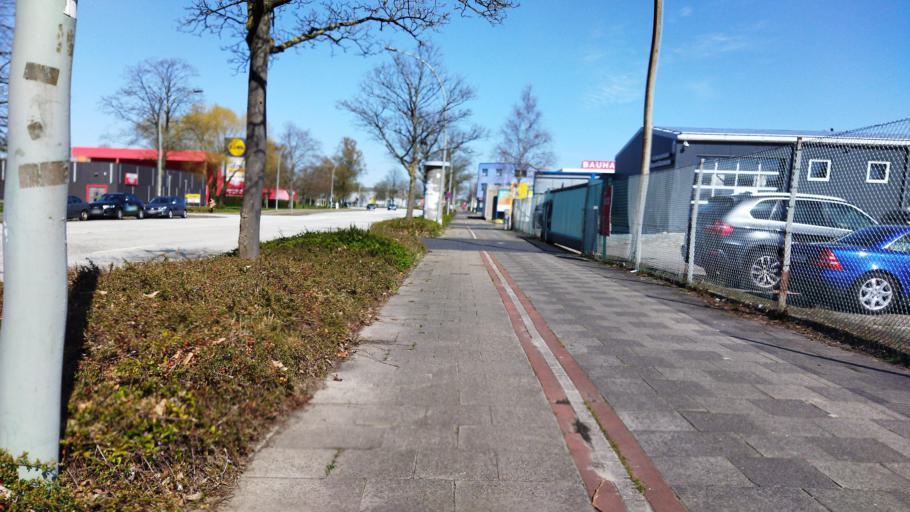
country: DE
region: Bremen
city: Bremerhaven
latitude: 53.5446
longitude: 8.5952
